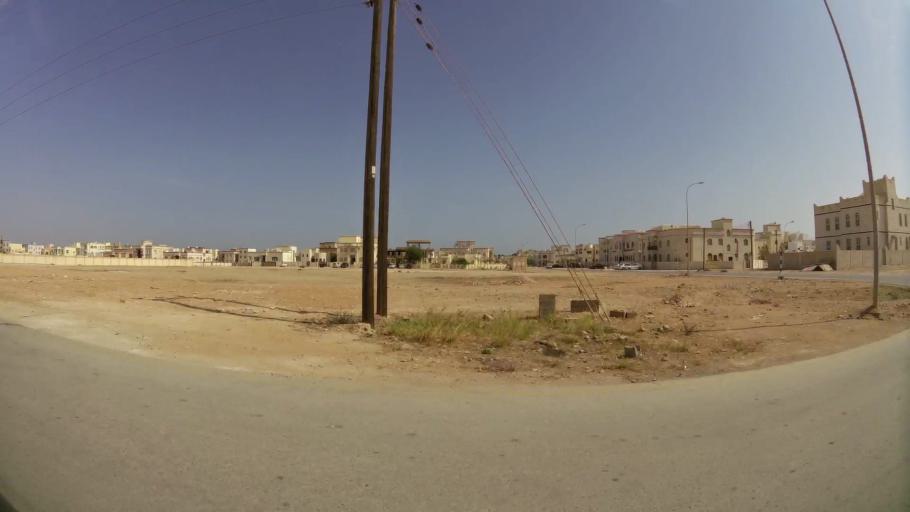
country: OM
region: Zufar
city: Salalah
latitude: 17.0448
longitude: 54.1516
